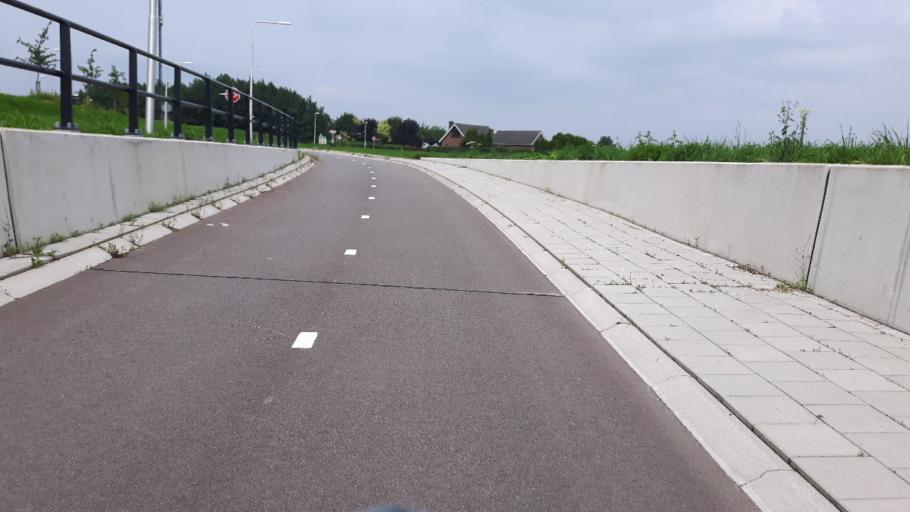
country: NL
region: Utrecht
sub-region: Gemeente Houten
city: Houten
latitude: 52.0406
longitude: 5.1859
